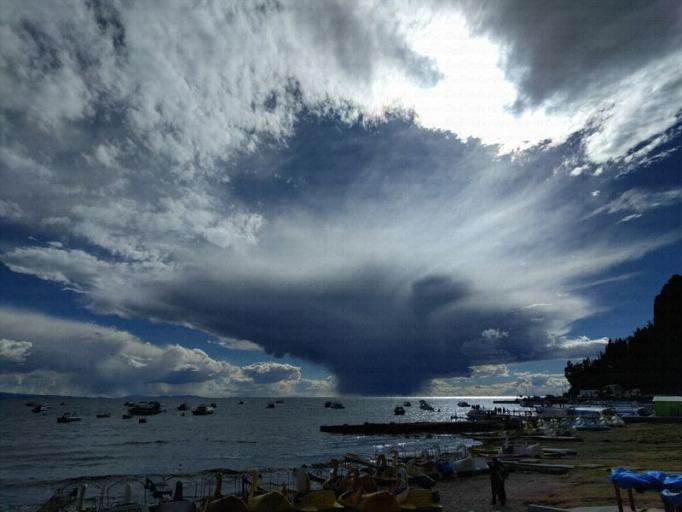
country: PE
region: Puno
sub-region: Yunguyo
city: Yunguyo
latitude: -16.1660
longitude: -69.0899
